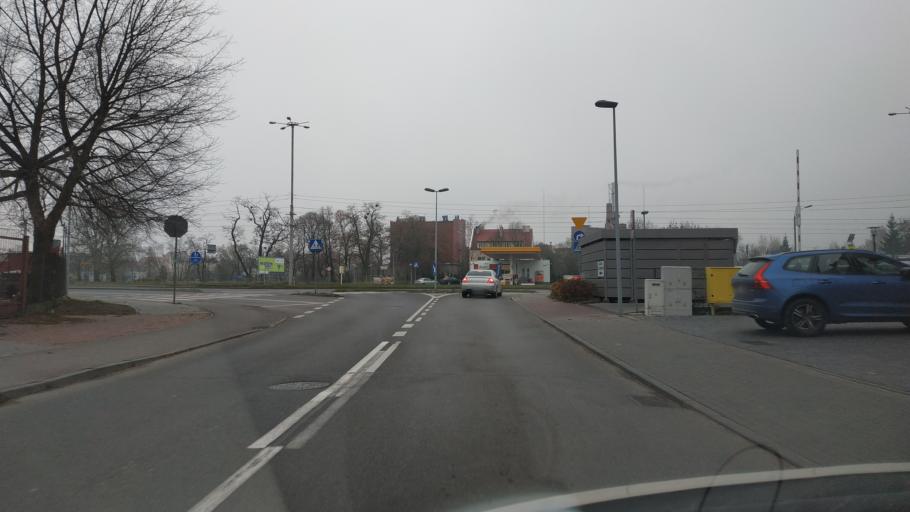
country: PL
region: Kujawsko-Pomorskie
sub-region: Torun
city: Torun
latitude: 53.0255
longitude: 18.6266
